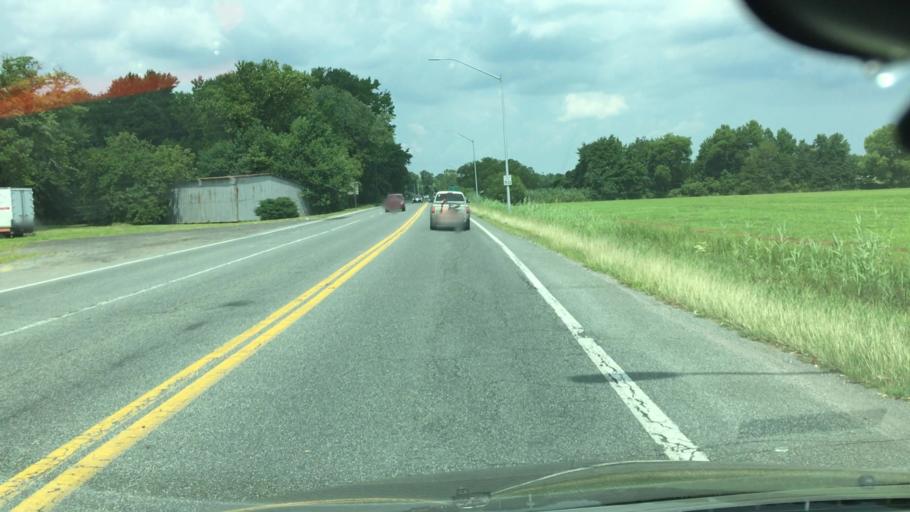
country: US
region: Maryland
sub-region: Worcester County
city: Ocean Pines
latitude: 38.3475
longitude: -75.1677
